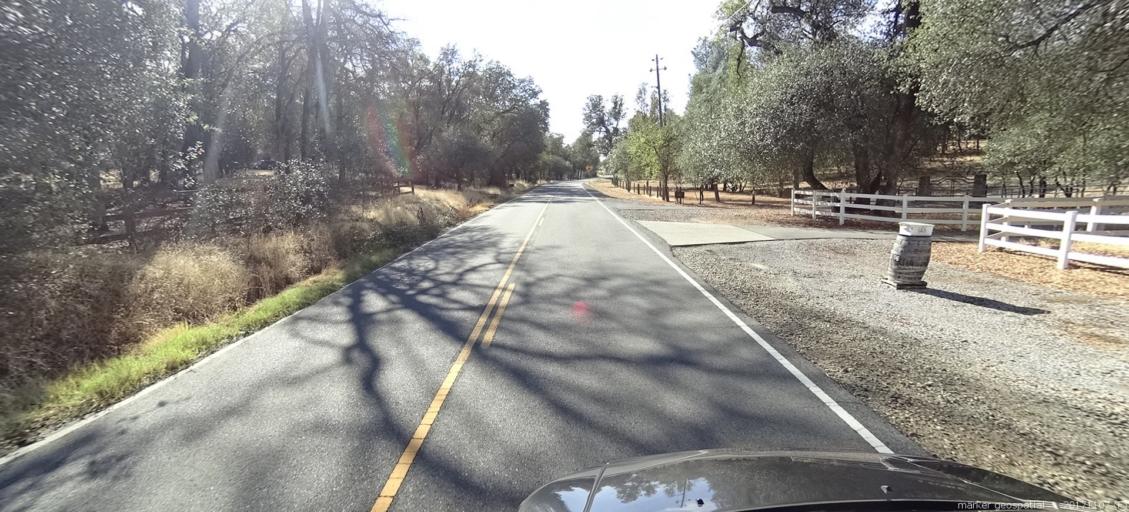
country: US
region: California
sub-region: Shasta County
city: Shasta
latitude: 40.4927
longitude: -122.5486
